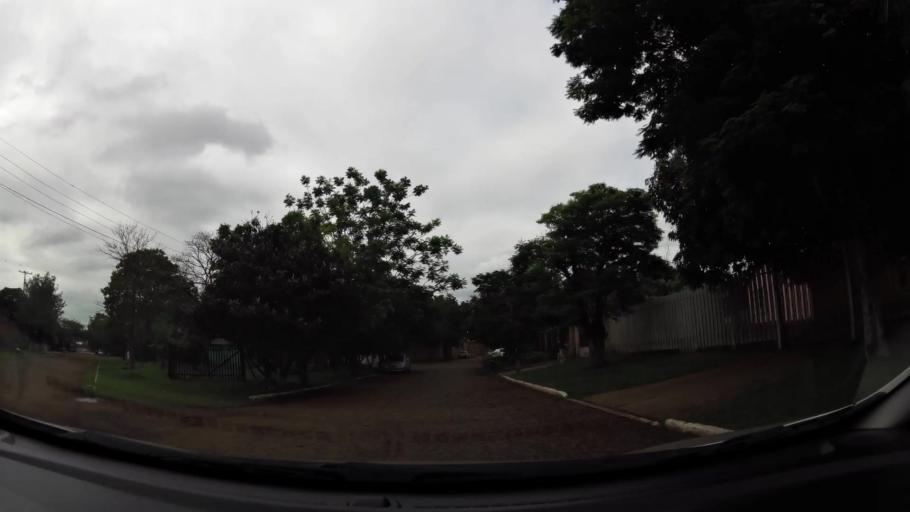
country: PY
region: Alto Parana
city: Ciudad del Este
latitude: -25.4093
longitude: -54.6364
